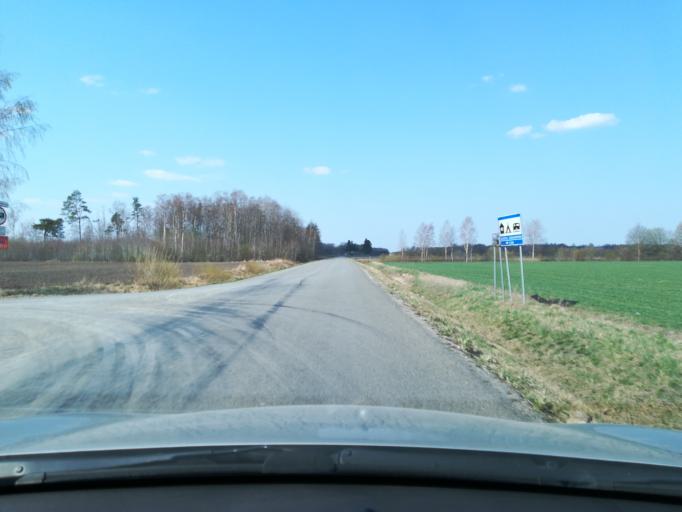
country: EE
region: Harju
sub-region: Saue linn
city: Saue
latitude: 59.3311
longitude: 24.5136
